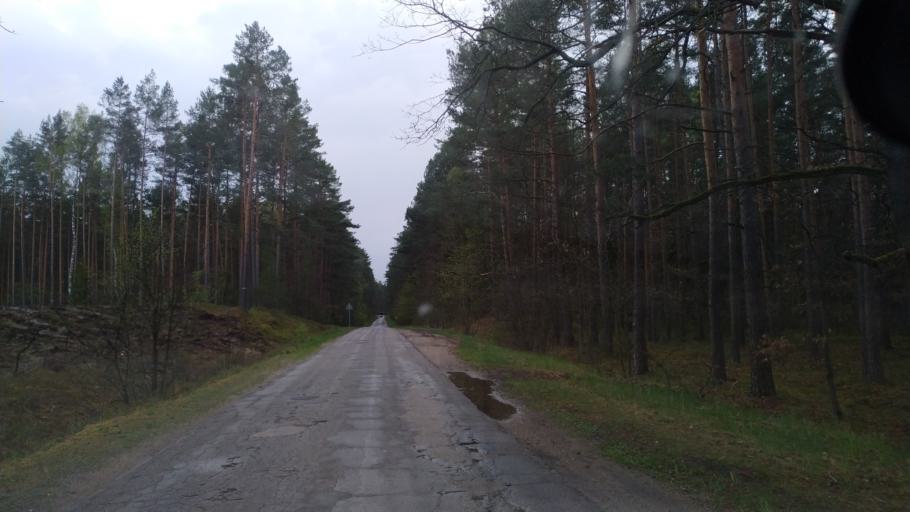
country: PL
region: Pomeranian Voivodeship
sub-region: Powiat starogardzki
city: Osiek
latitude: 53.6875
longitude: 18.5115
